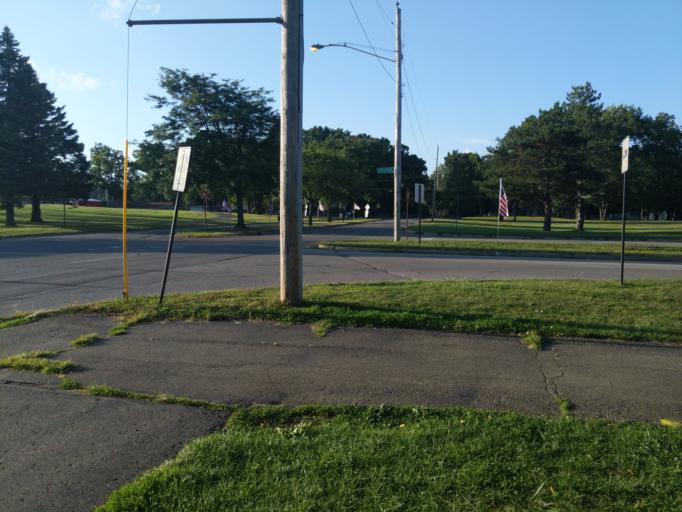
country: US
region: Michigan
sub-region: Jackson County
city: Jackson
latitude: 42.2316
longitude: -84.4327
